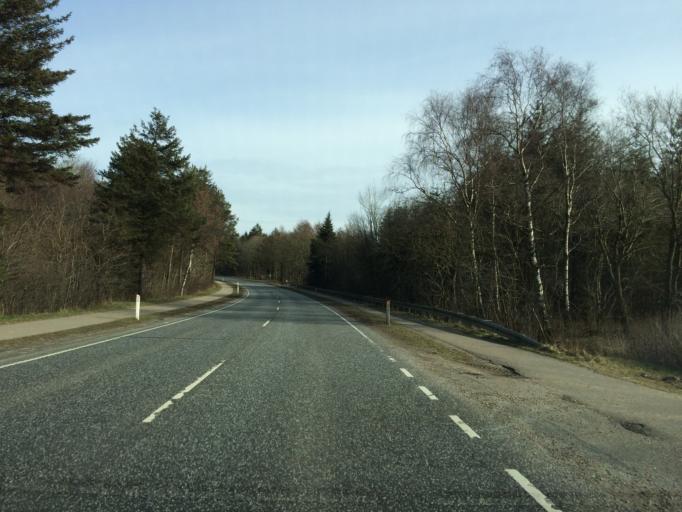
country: DK
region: Central Jutland
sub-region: Holstebro Kommune
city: Holstebro
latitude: 56.3426
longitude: 8.6188
